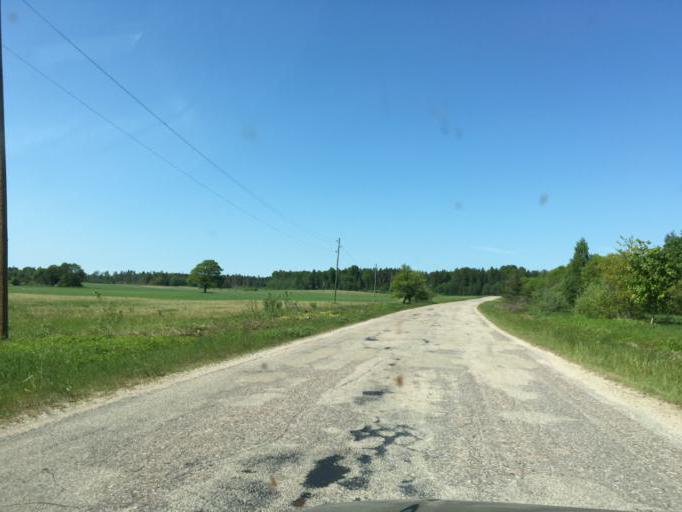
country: LV
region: Dundaga
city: Dundaga
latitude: 57.4703
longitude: 22.3220
